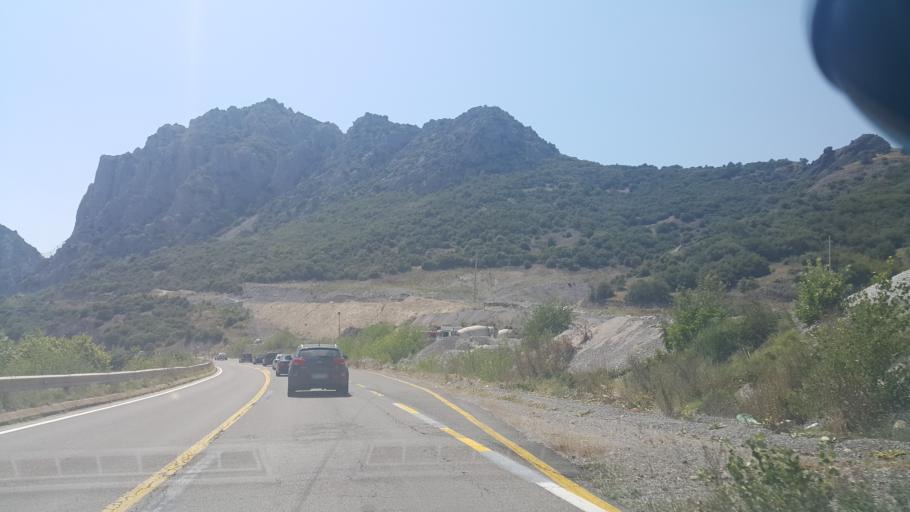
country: MK
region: Demir Kapija
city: Demir Kapija
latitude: 41.4105
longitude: 22.2729
